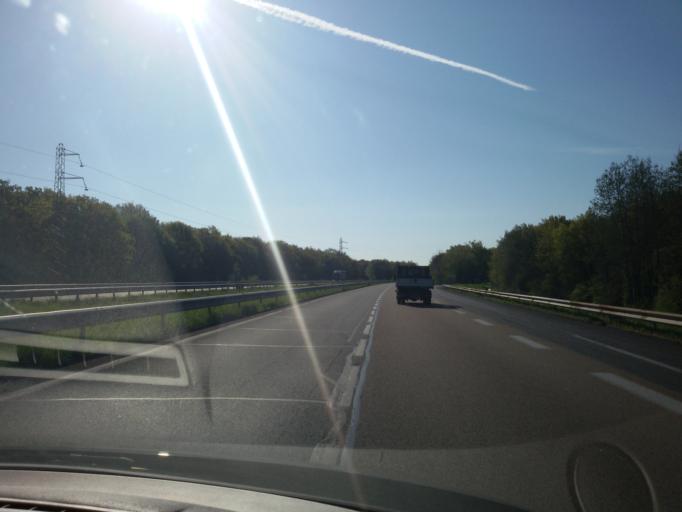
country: FR
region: Centre
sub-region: Departement du Loiret
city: Courtenay
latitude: 48.1080
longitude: 3.0124
